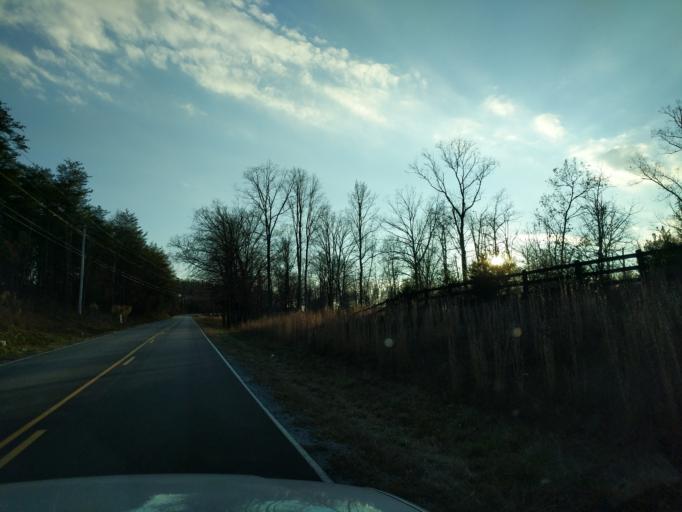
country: US
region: North Carolina
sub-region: Polk County
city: Columbus
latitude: 35.2688
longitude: -82.0575
